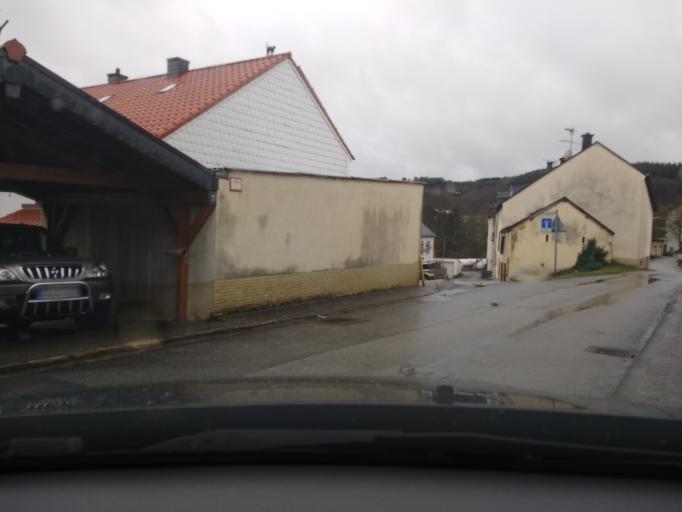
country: DE
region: Rheinland-Pfalz
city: Irsch
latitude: 49.7240
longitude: 6.6847
